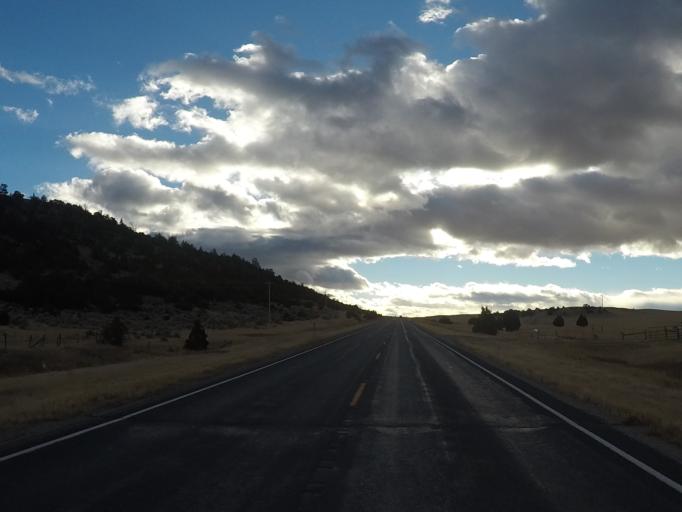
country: US
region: Montana
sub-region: Jefferson County
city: Whitehall
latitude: 45.9029
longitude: -111.9514
